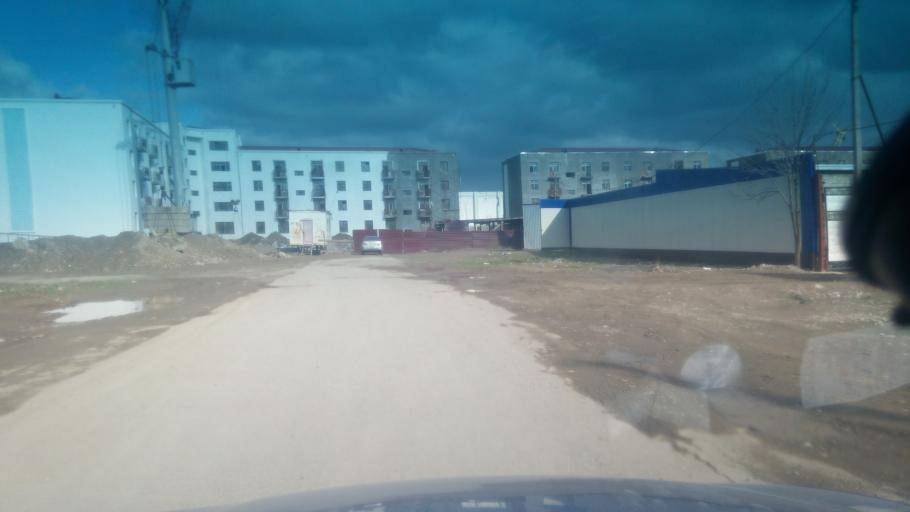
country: UZ
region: Sirdaryo
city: Guliston
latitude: 40.5082
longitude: 68.7648
